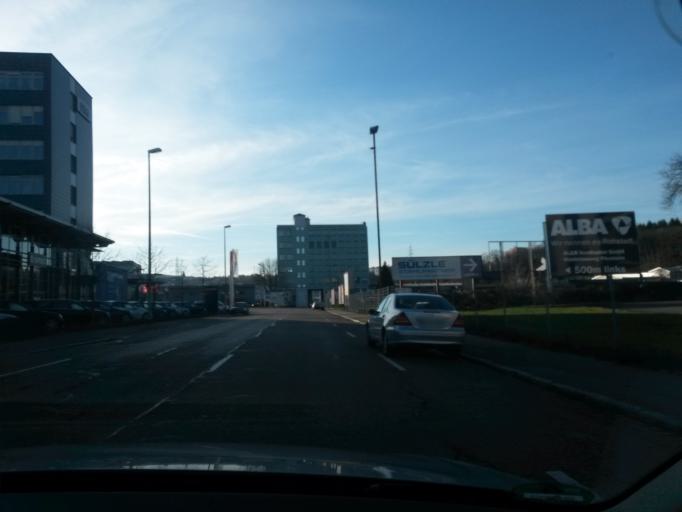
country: DE
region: Baden-Wuerttemberg
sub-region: Karlsruhe Region
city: Birkenfeld
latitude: 48.8807
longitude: 8.6561
